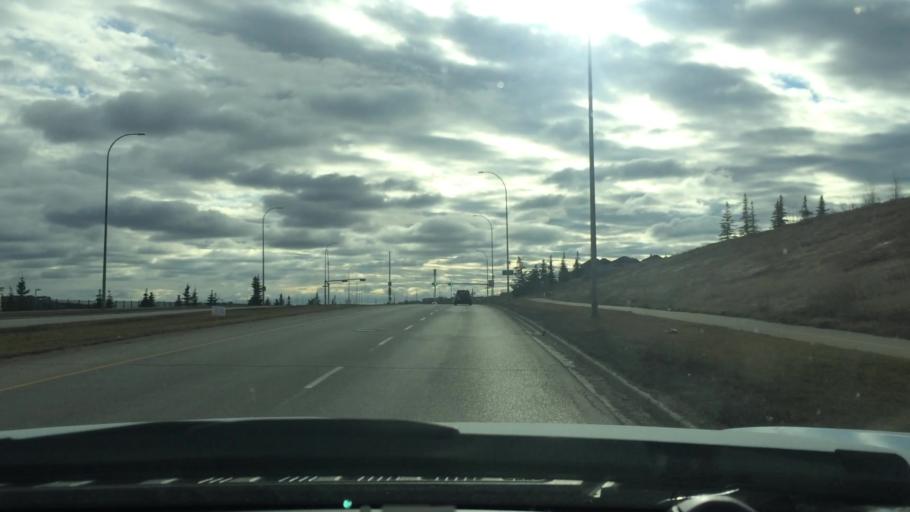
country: CA
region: Alberta
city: Calgary
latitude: 51.1627
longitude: -114.1274
